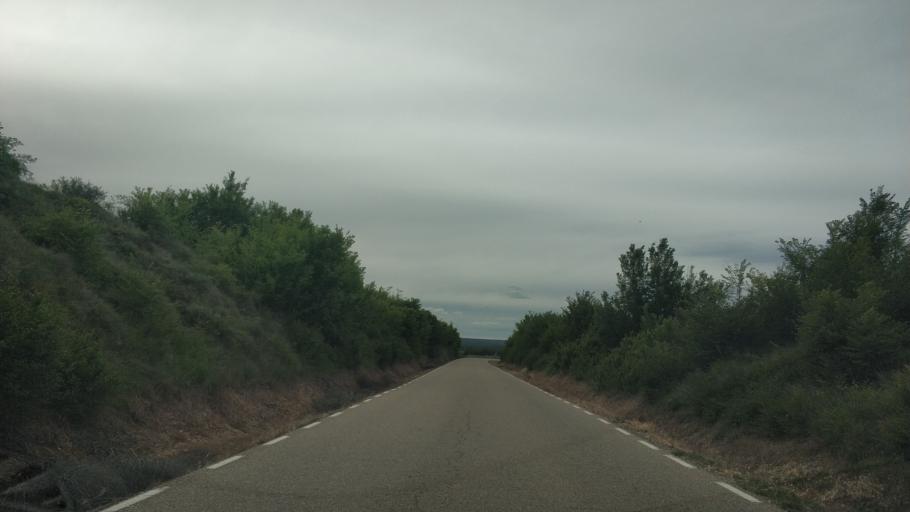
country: ES
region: Castille and Leon
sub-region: Provincia de Soria
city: Berlanga de Duero
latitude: 41.4801
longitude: -2.8631
